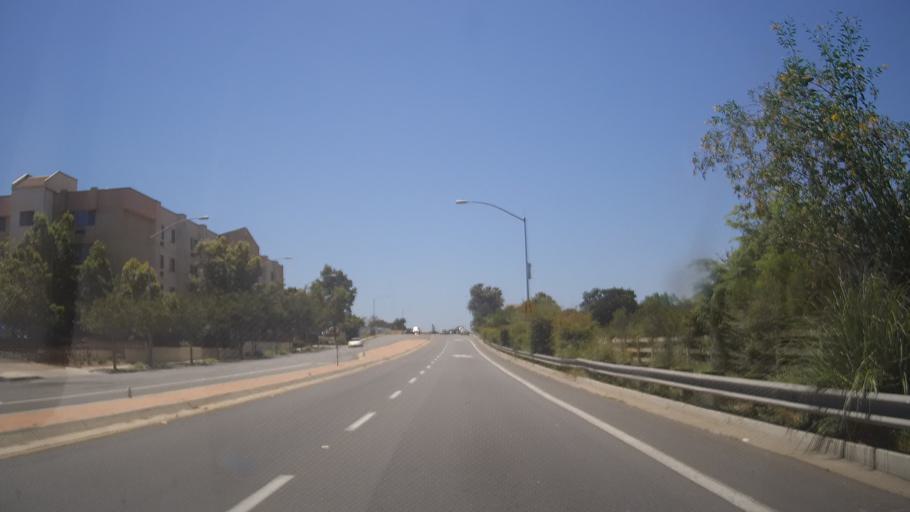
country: US
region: California
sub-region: San Diego County
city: National City
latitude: 32.7085
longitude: -117.0737
